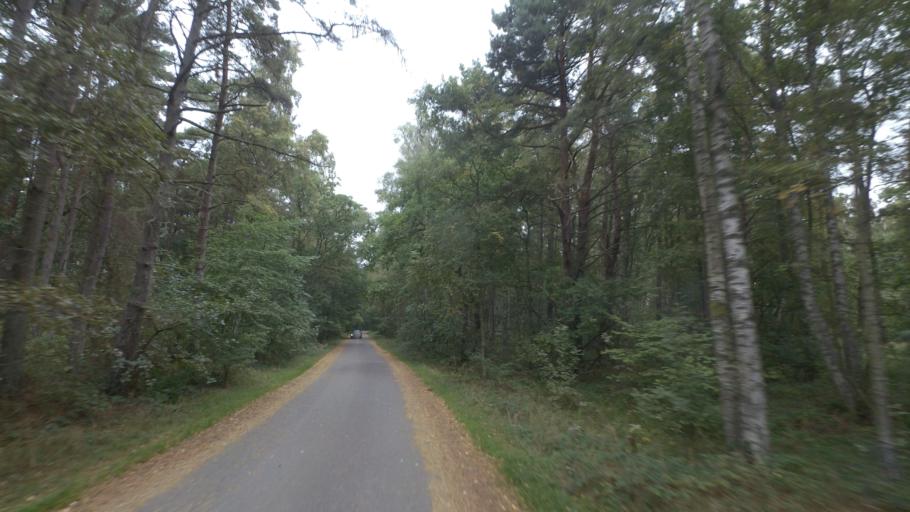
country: DK
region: Capital Region
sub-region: Bornholm Kommune
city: Nexo
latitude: 55.0003
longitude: 15.0388
